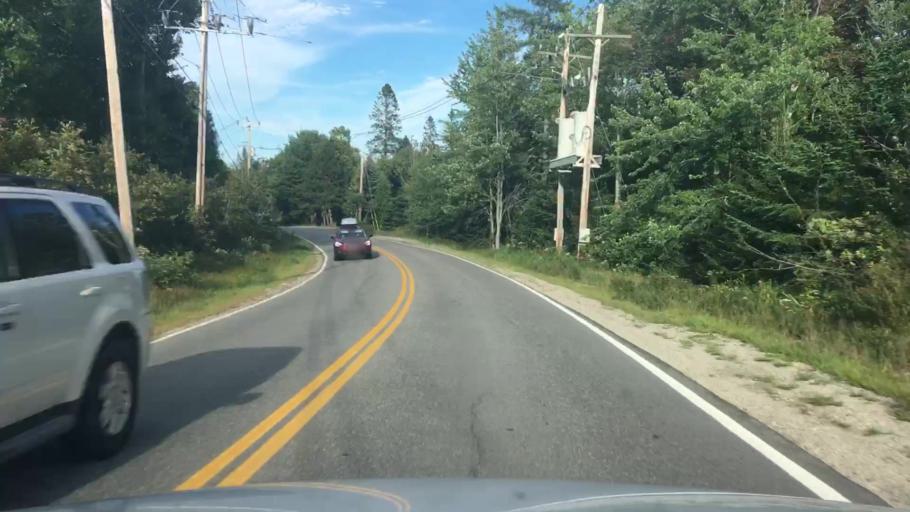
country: US
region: Maine
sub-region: Hancock County
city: Trenton
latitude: 44.4376
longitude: -68.3733
